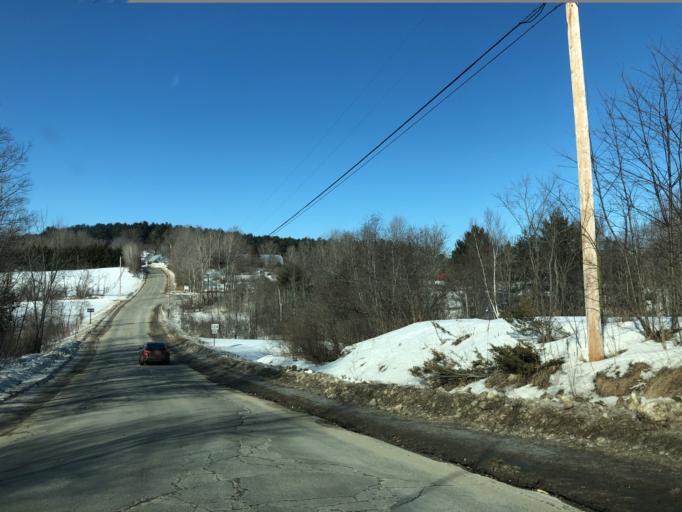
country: US
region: Maine
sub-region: Oxford County
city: Buckfield
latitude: 44.2585
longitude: -70.3372
